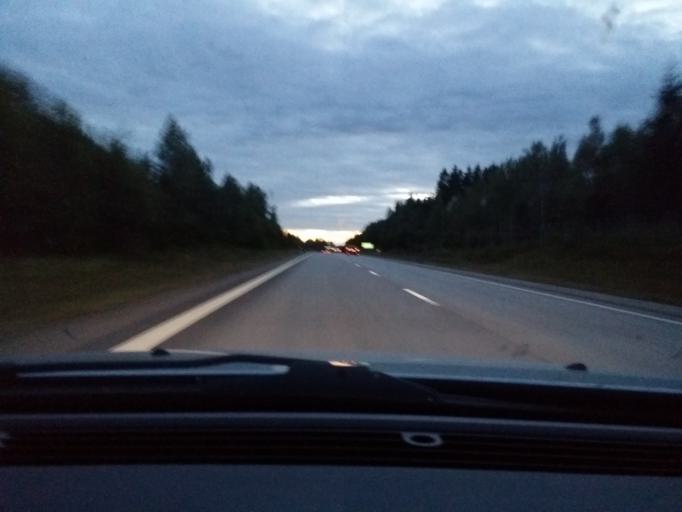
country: SE
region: Uppsala
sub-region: Enkopings Kommun
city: Grillby
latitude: 59.6460
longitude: 17.1707
